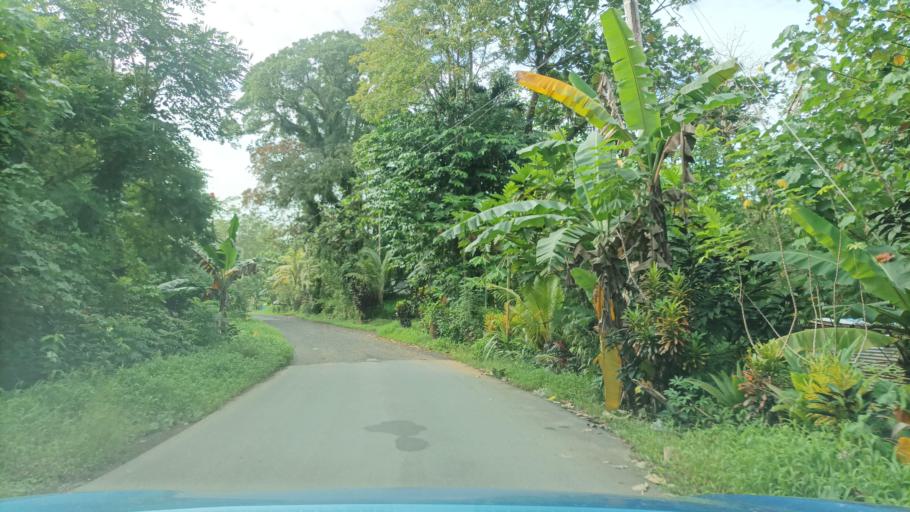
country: FM
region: Pohnpei
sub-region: Kolonia Municipality
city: Kolonia
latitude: 6.9443
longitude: 158.2243
